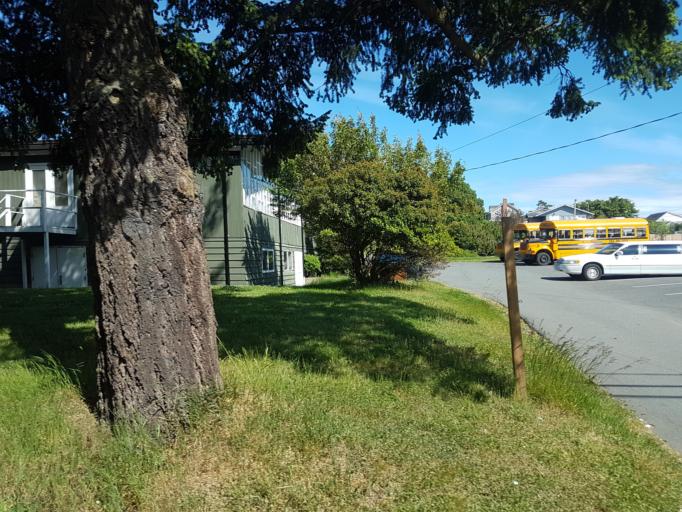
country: CA
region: British Columbia
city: Oak Bay
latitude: 48.4833
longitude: -123.3214
